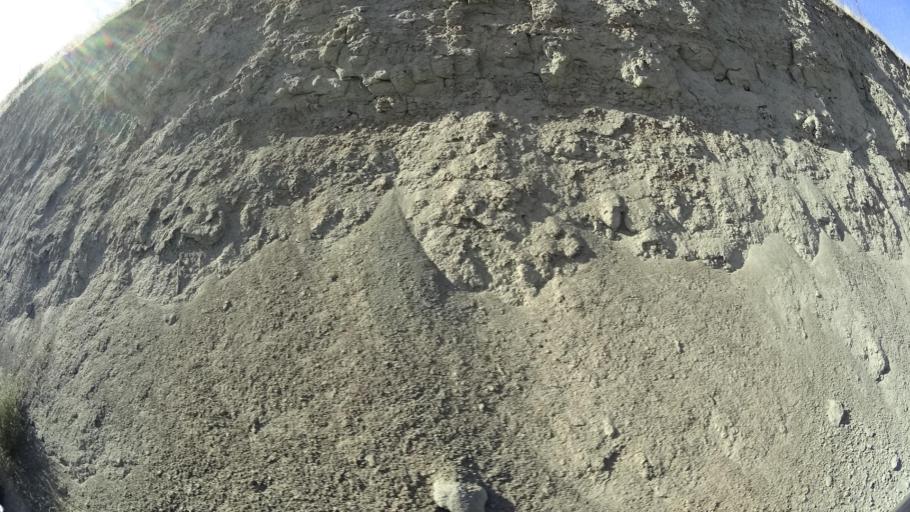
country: US
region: California
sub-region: Kern County
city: Oildale
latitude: 35.5514
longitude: -118.9587
